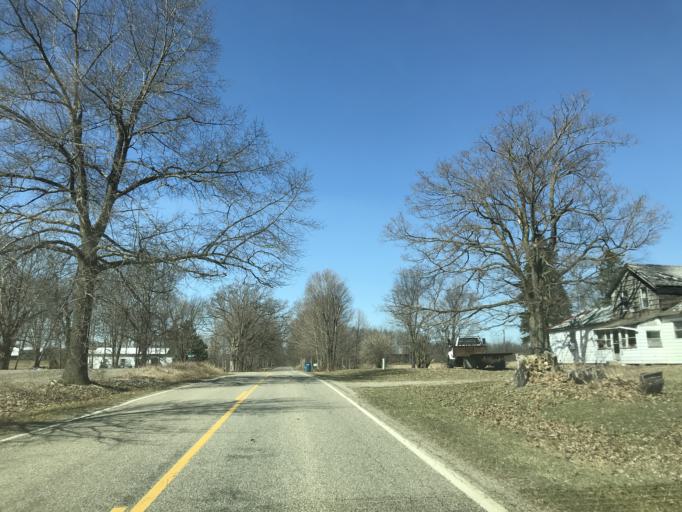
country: US
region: Michigan
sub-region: Hillsdale County
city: Litchfield
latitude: 41.9855
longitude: -84.7375
